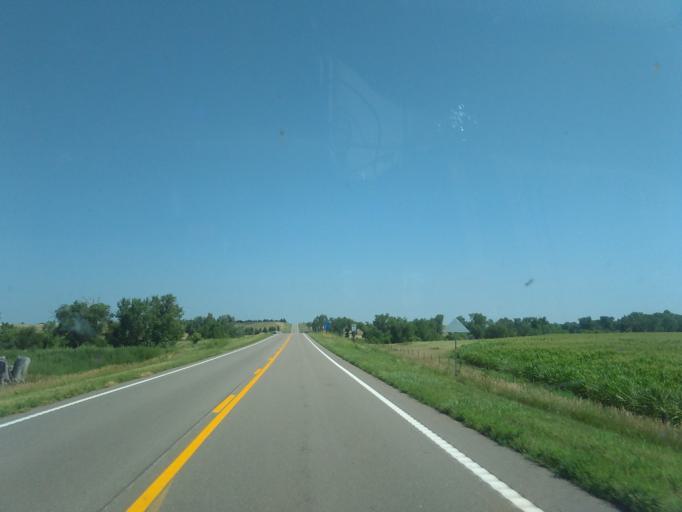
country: US
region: Nebraska
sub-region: Dundy County
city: Benkelman
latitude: 40.0077
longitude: -101.5424
